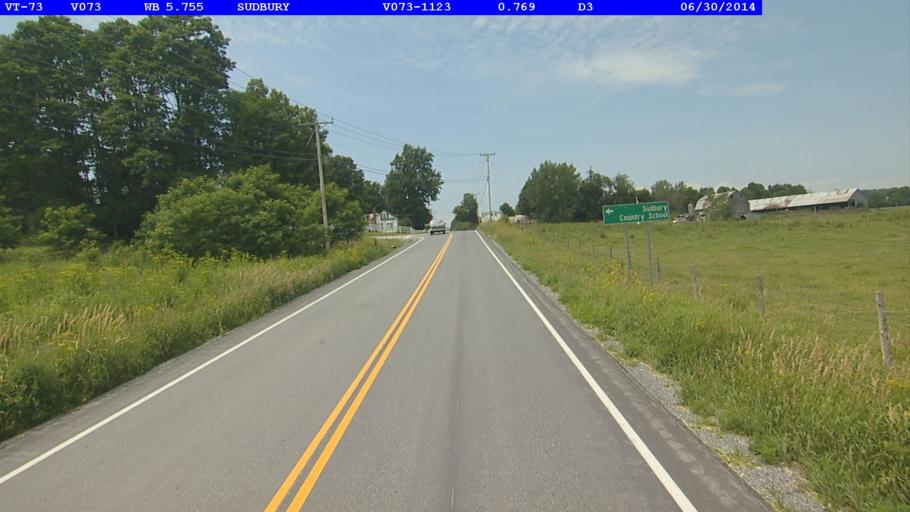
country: US
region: Vermont
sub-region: Rutland County
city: Brandon
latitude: 43.8233
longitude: -73.1853
